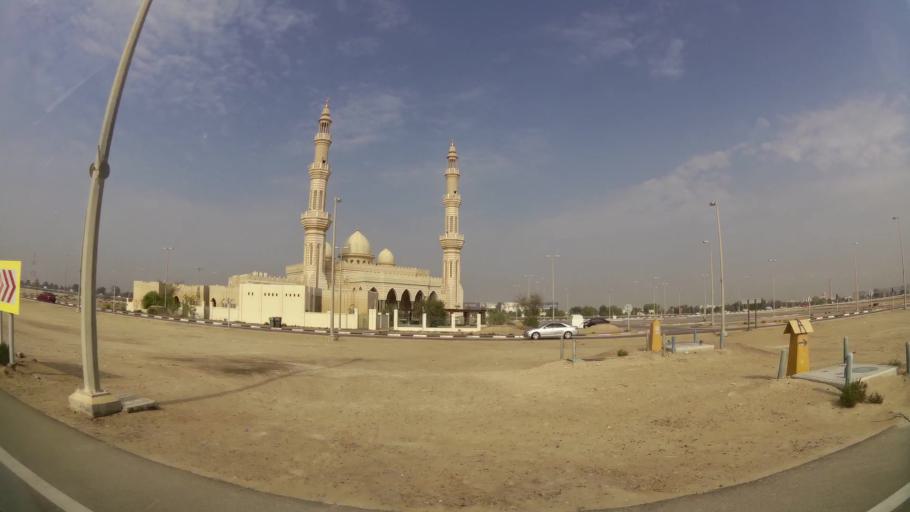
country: AE
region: Abu Dhabi
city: Abu Dhabi
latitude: 24.6643
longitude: 54.7610
